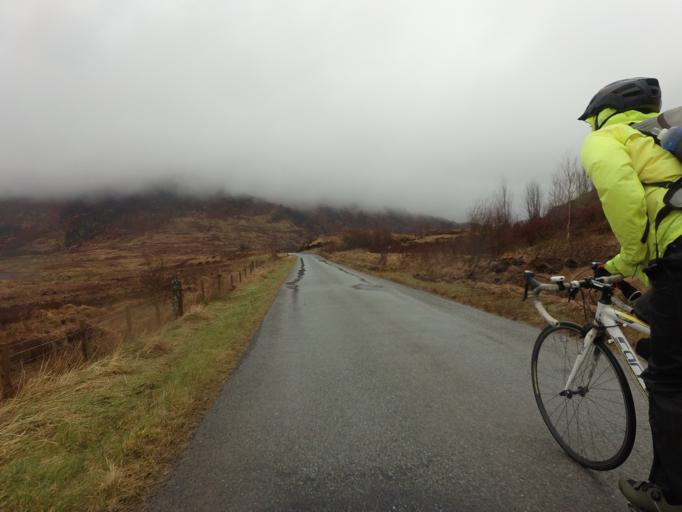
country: GB
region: Scotland
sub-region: West Dunbartonshire
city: Balloch
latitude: 56.2495
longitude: -4.5869
